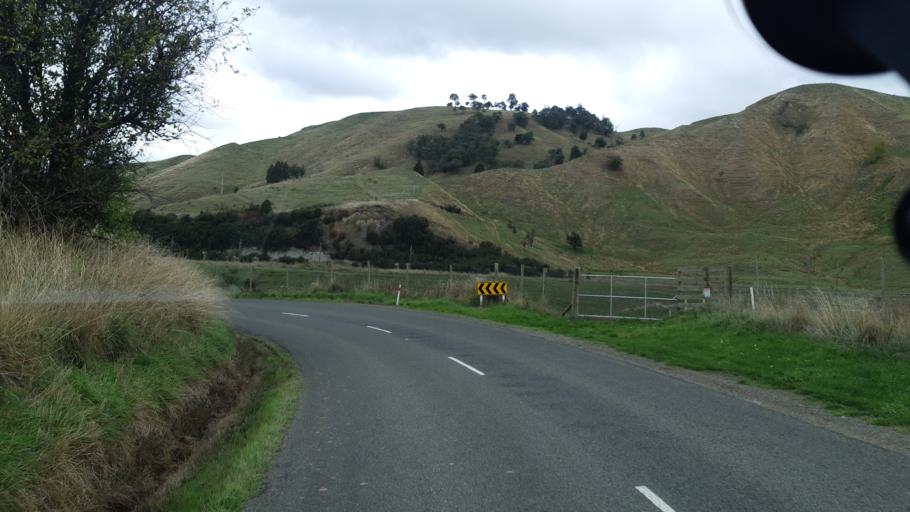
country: NZ
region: Manawatu-Wanganui
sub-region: Ruapehu District
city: Waiouru
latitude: -39.6507
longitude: 175.7444
